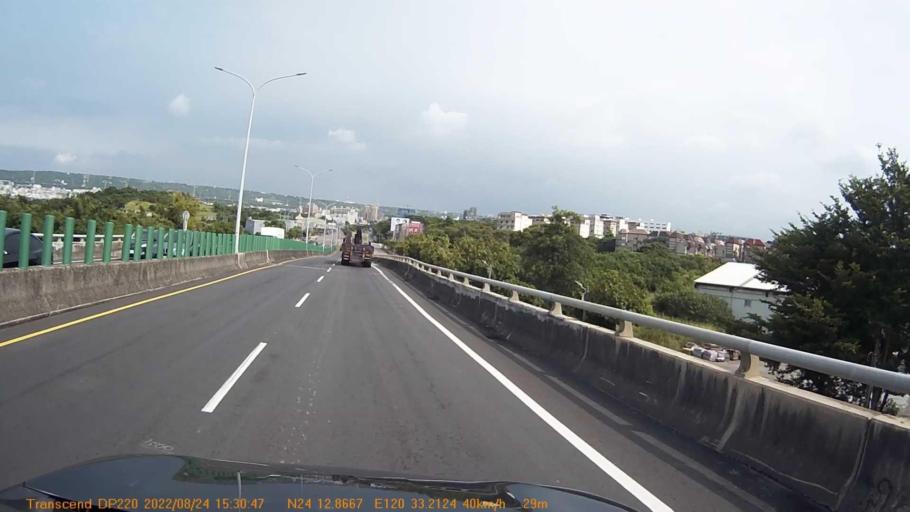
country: TW
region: Taiwan
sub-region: Changhua
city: Chang-hua
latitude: 24.2142
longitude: 120.5539
